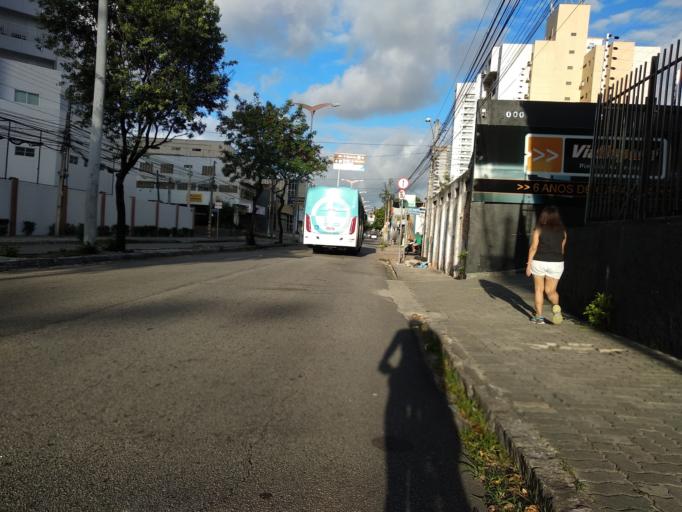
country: BR
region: Ceara
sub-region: Fortaleza
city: Fortaleza
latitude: -3.7363
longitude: -38.5160
